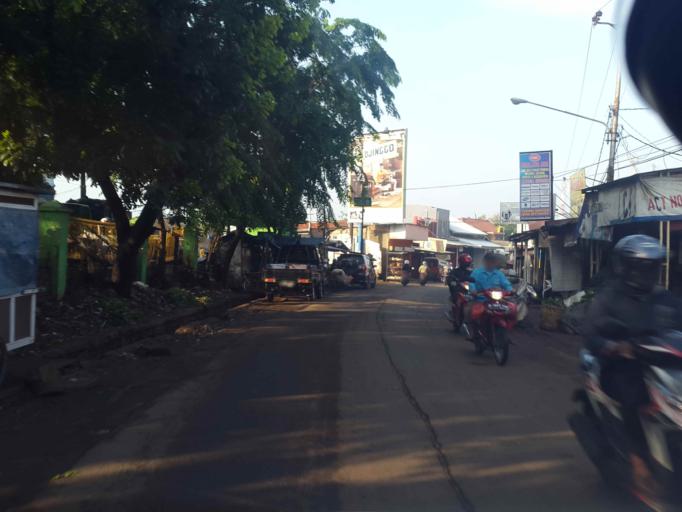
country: ID
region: West Java
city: Cileungsir
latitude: -6.3359
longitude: 107.0451
